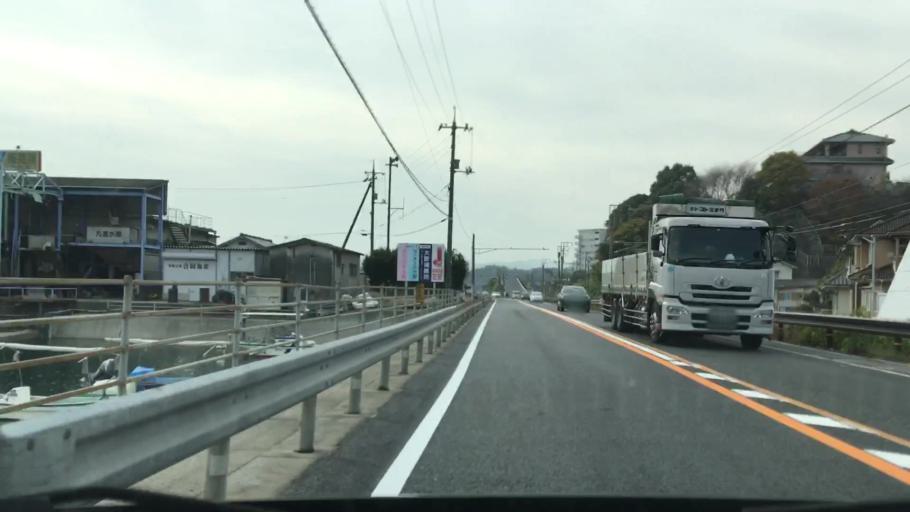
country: JP
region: Hiroshima
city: Ono-hara
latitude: 34.2739
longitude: 132.2595
